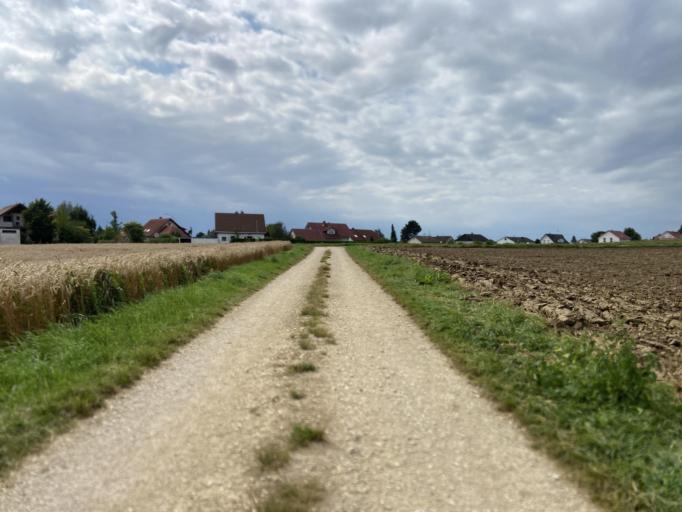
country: DE
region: Baden-Wuerttemberg
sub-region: Tuebingen Region
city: Bingen
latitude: 48.1169
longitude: 9.2749
